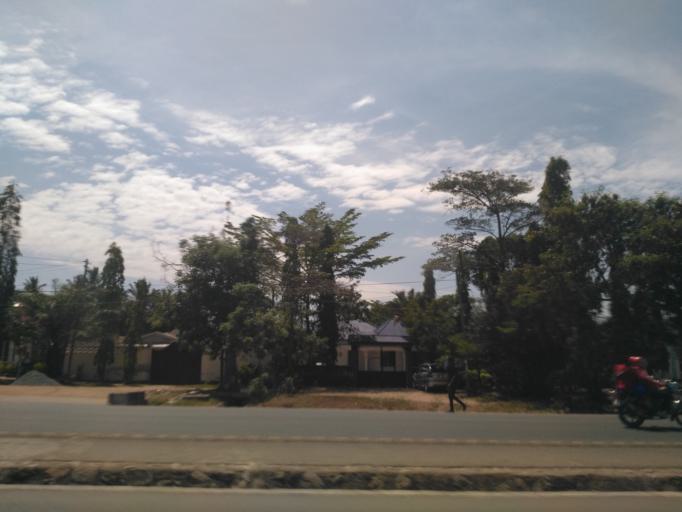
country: TZ
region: Mwanza
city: Mwanza
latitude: -2.4893
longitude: 32.9060
